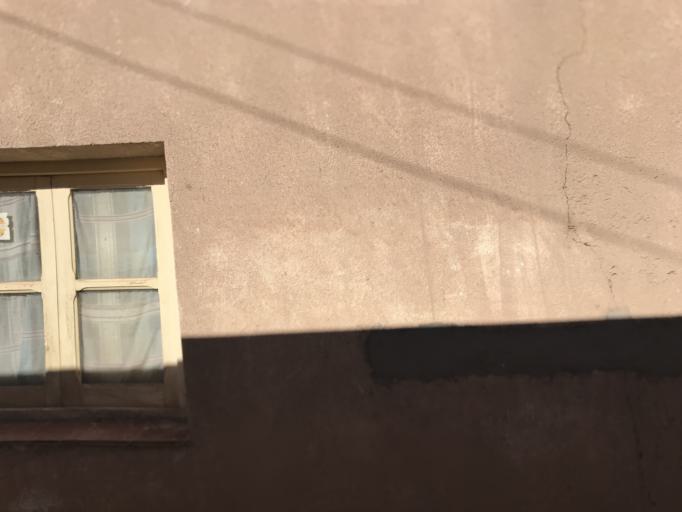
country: AR
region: Jujuy
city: Maimara
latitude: -23.6260
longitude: -65.4084
